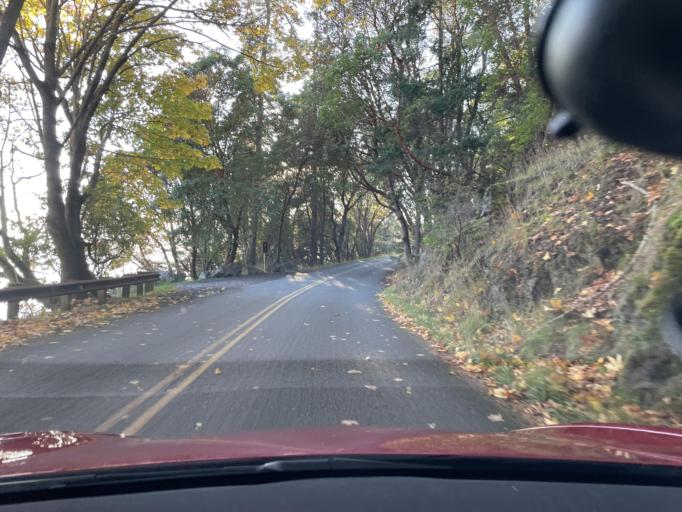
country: US
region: Washington
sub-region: San Juan County
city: Friday Harbor
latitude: 48.5140
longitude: -123.1443
